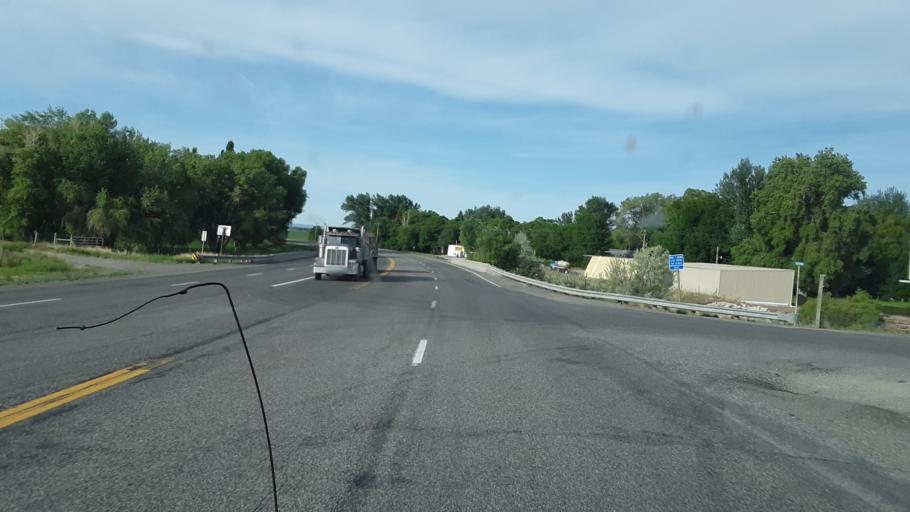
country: US
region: Wyoming
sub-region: Fremont County
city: Riverton
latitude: 43.0823
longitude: -108.3795
